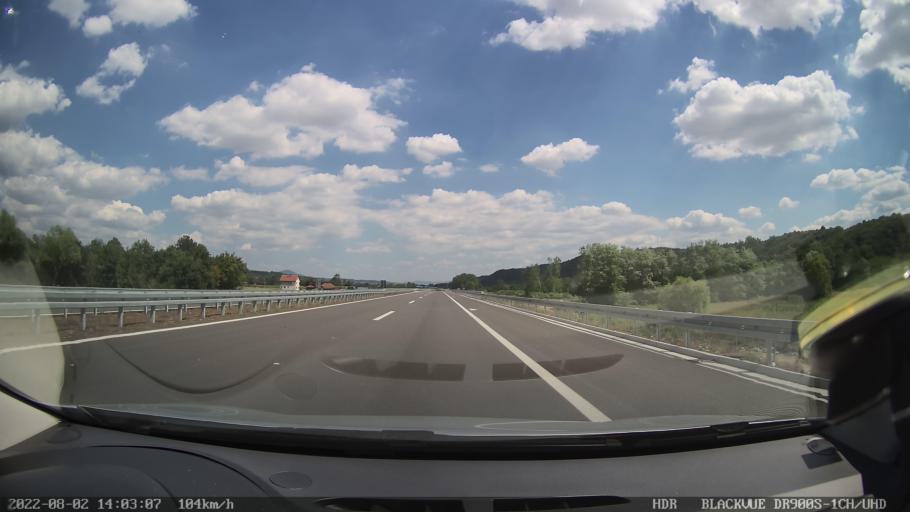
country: RS
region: Central Serbia
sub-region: Moravicki Okrug
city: Cacak
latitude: 43.9274
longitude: 20.3426
